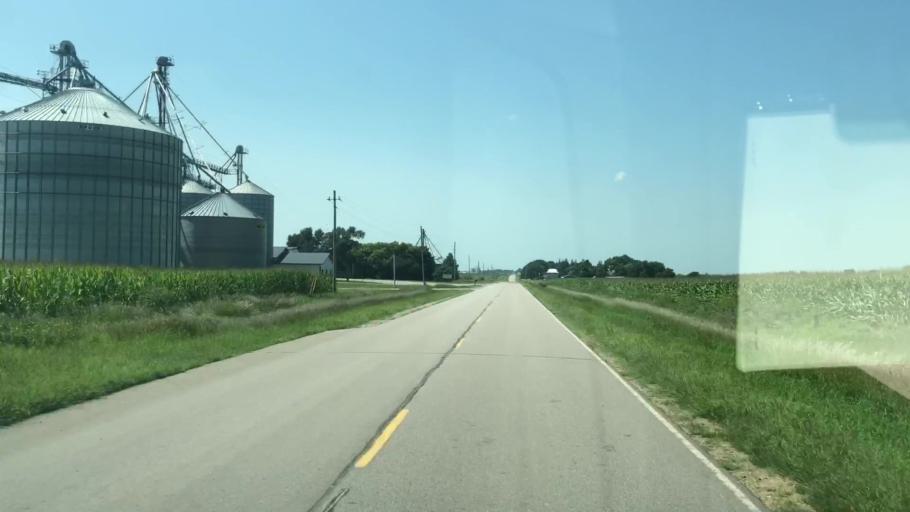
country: US
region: Iowa
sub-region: O'Brien County
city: Sheldon
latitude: 43.2443
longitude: -95.7734
